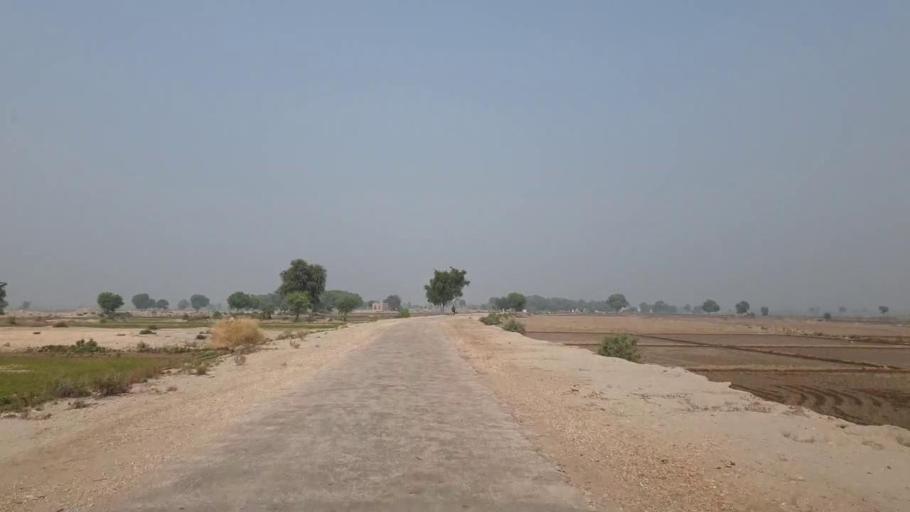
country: PK
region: Sindh
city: Bhan
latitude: 26.5180
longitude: 67.6898
